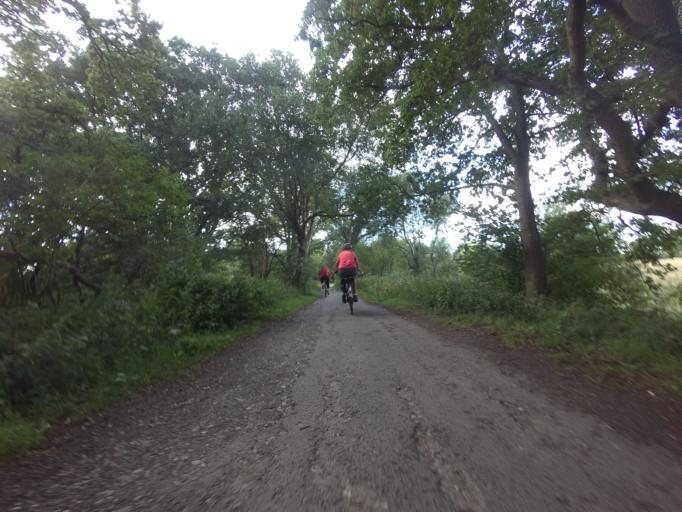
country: GB
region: England
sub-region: East Sussex
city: Horam
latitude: 50.9281
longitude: 0.2514
